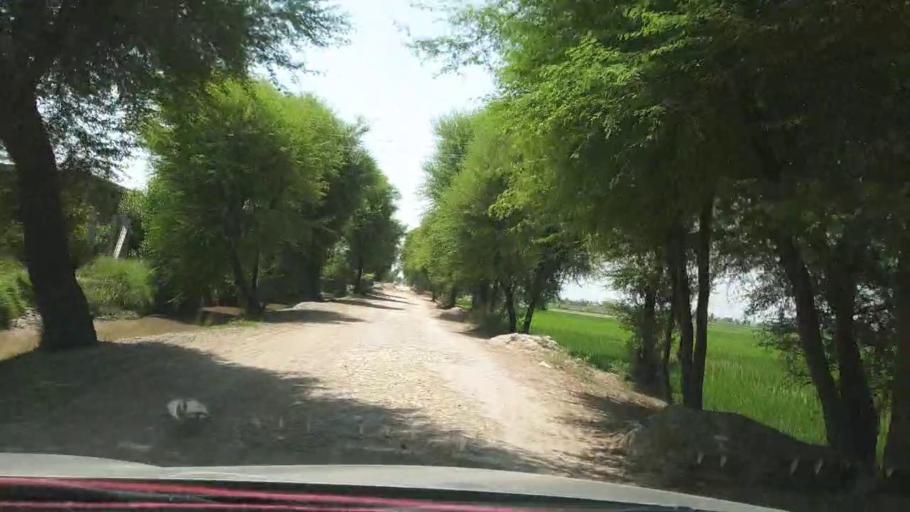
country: PK
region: Sindh
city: Warah
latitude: 27.5040
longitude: 67.7860
